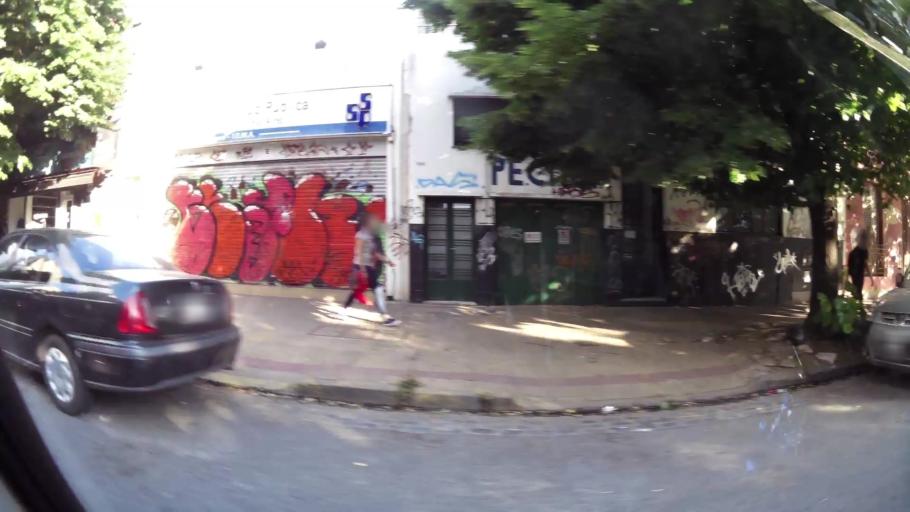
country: AR
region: Buenos Aires
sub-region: Partido de La Plata
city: La Plata
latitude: -34.9124
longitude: -57.9570
